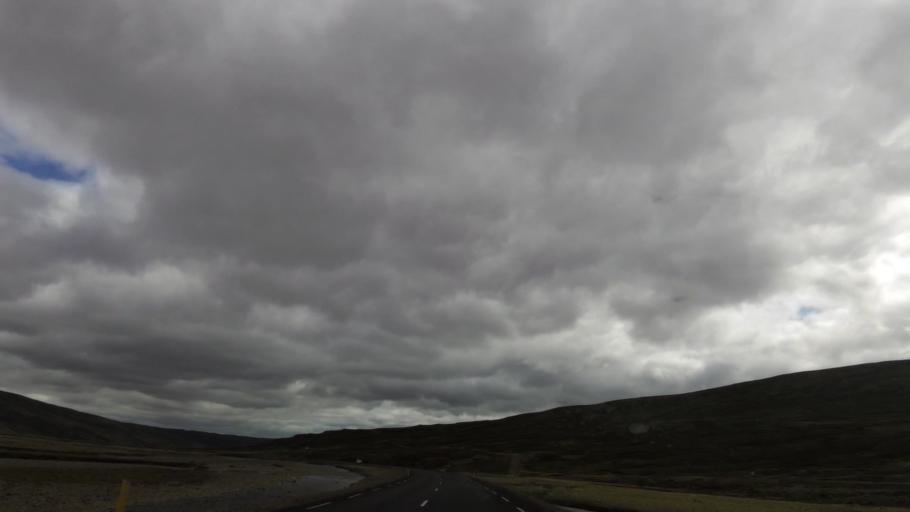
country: IS
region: West
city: Stykkisholmur
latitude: 65.7581
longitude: -21.8679
